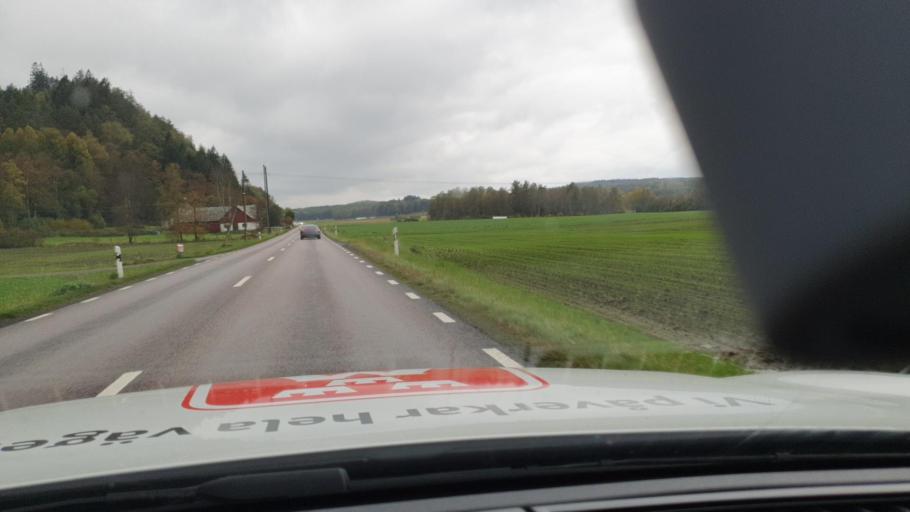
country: SE
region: Halland
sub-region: Falkenbergs Kommun
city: Falkenberg
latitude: 57.0515
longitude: 12.6122
